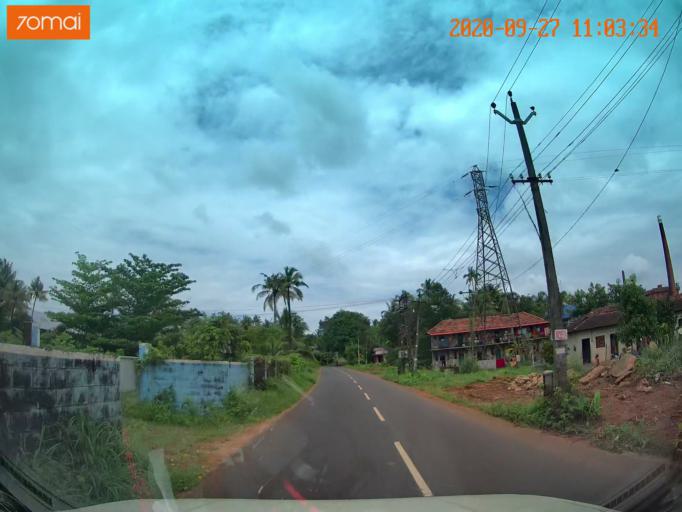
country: IN
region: Kerala
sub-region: Thrissur District
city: Irinjalakuda
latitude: 10.4219
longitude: 76.2559
